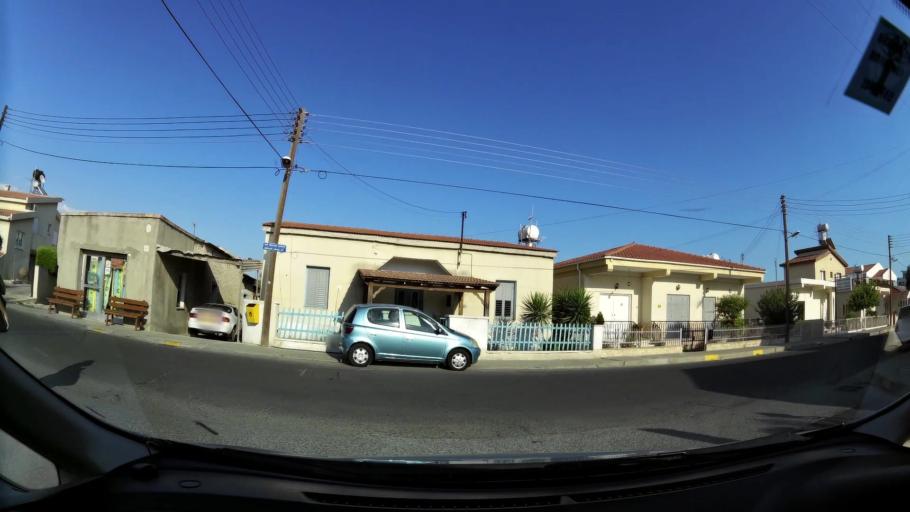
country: CY
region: Larnaka
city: Aradippou
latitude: 34.9494
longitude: 33.5932
